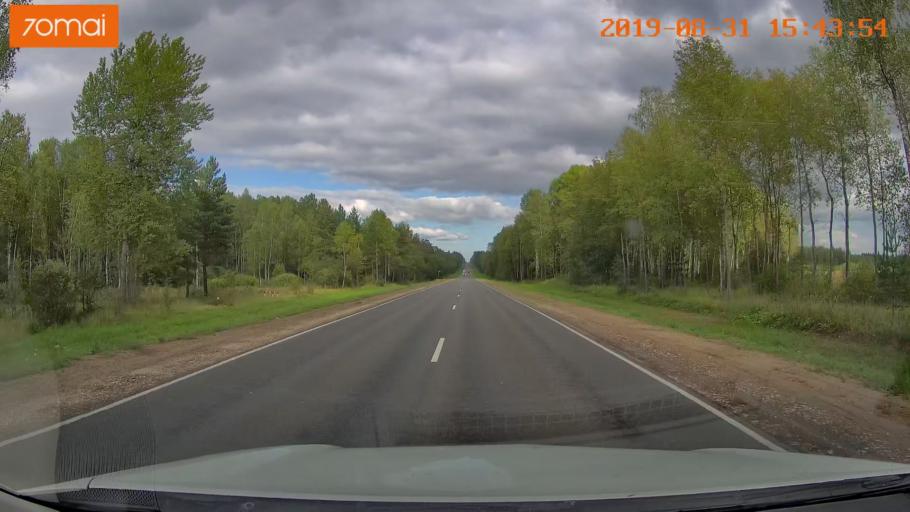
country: RU
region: Kaluga
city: Mosal'sk
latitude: 54.6554
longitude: 34.9196
